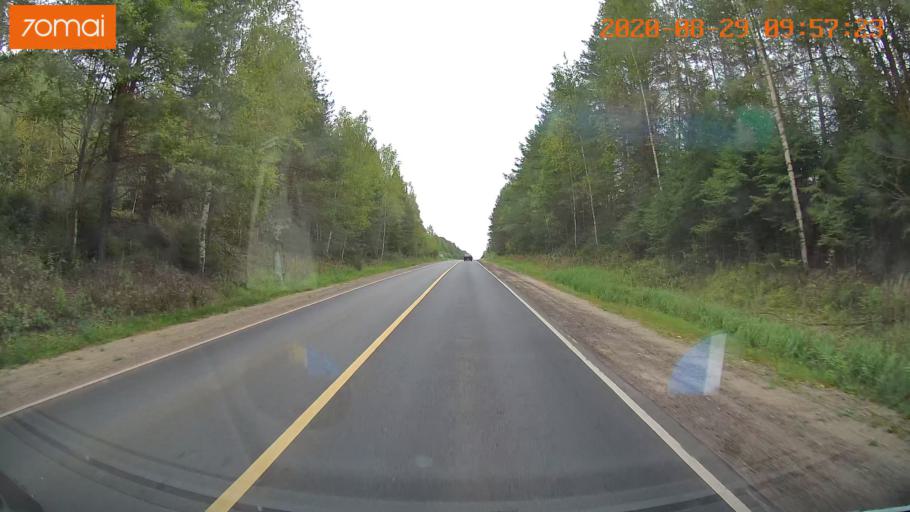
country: RU
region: Ivanovo
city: Zarechnyy
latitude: 57.4166
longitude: 42.3125
